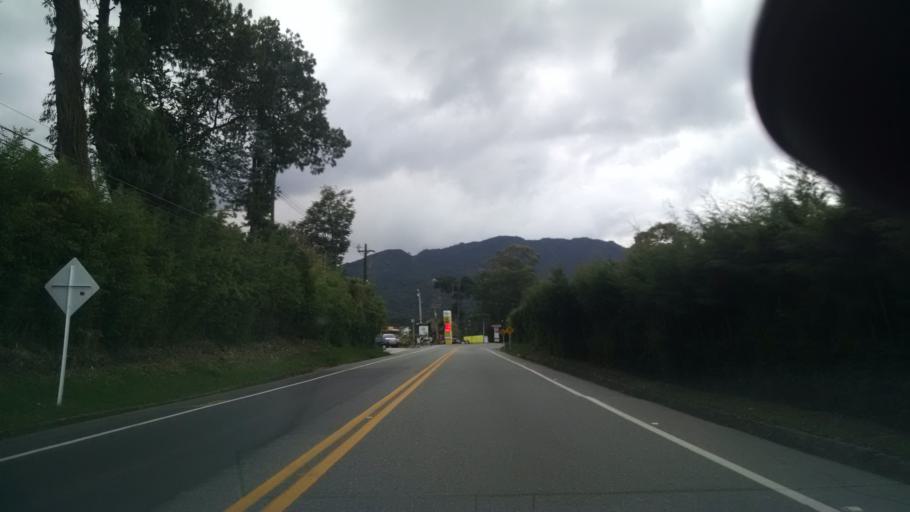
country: CO
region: Antioquia
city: El Retiro
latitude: 6.0947
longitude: -75.4998
